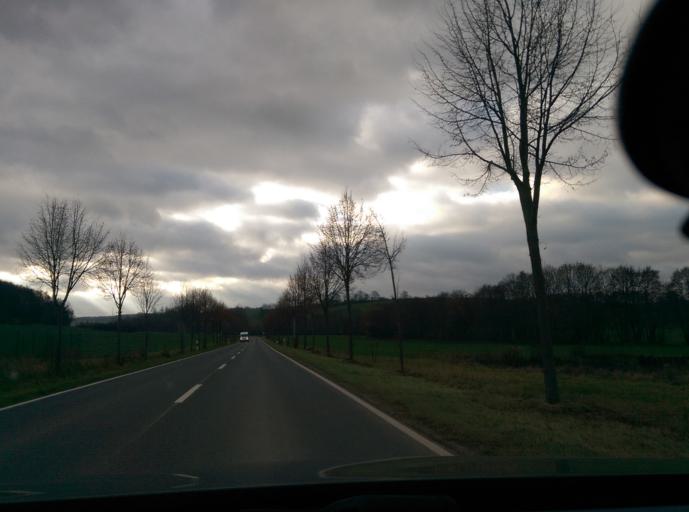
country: DE
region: Thuringia
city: Creuzburg
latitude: 51.0374
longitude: 10.2516
